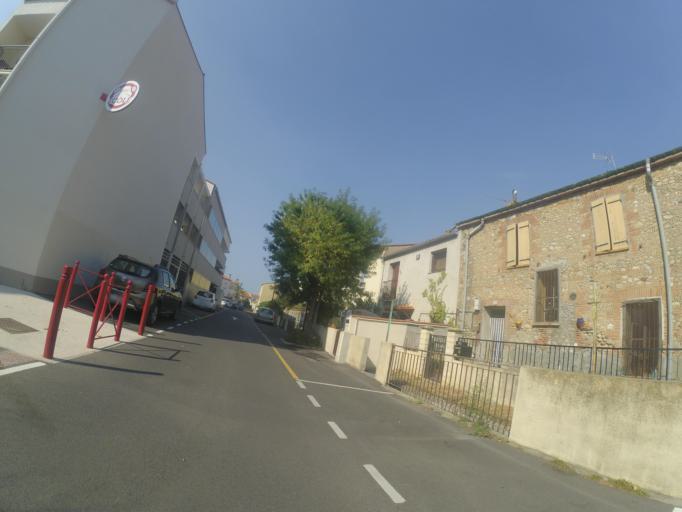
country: FR
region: Languedoc-Roussillon
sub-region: Departement des Pyrenees-Orientales
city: Toulouges
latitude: 42.6687
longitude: 2.8311
